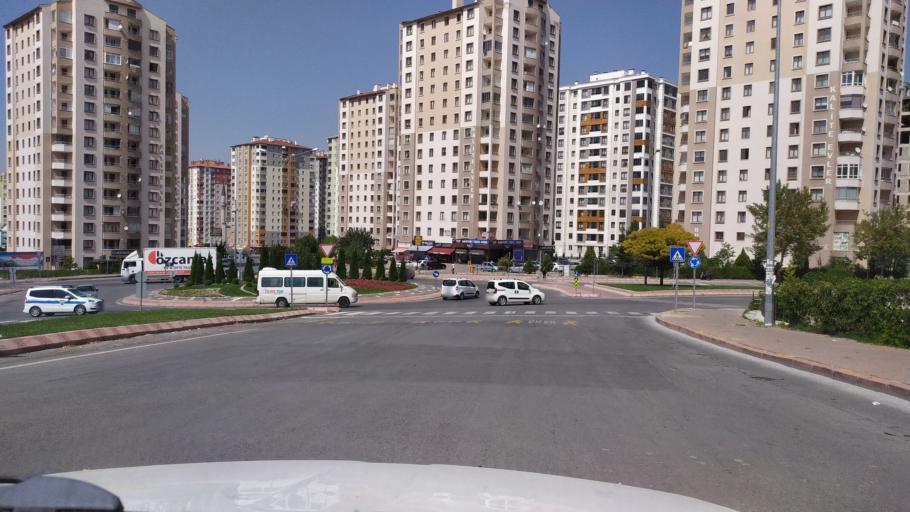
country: TR
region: Kayseri
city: Talas
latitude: 38.7080
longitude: 35.5609
